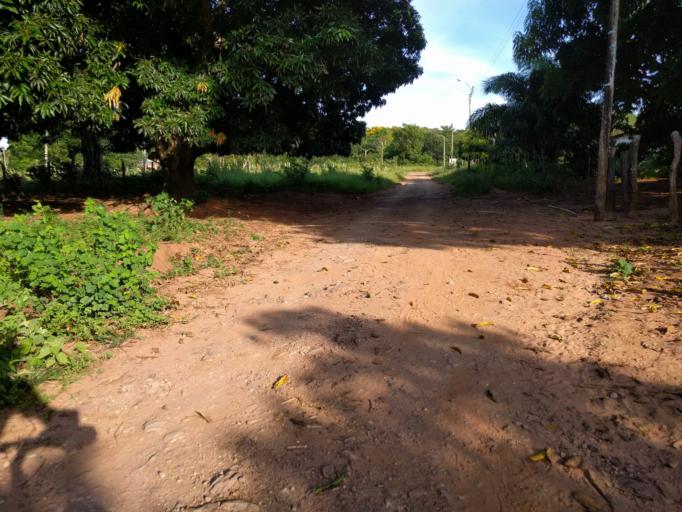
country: BO
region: Santa Cruz
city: Robore
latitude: -18.3339
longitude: -59.5902
